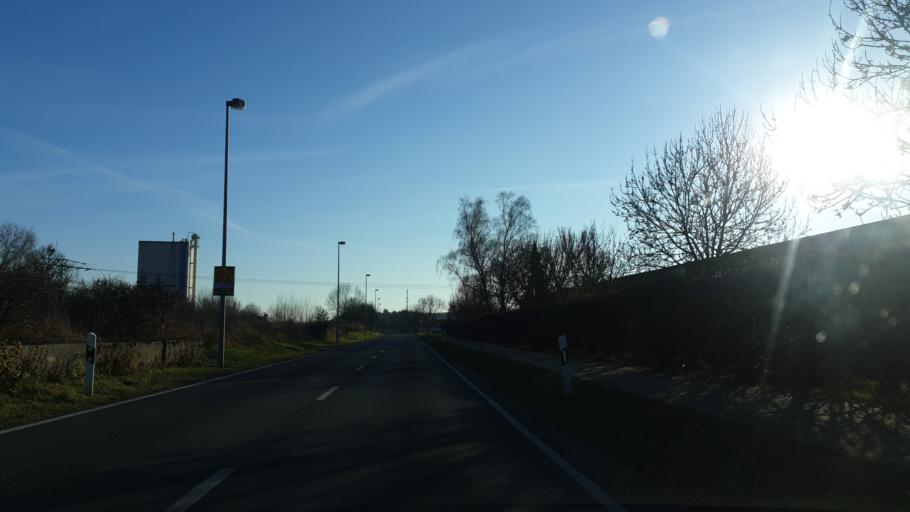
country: DE
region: Thuringia
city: Hartmannsdorf
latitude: 50.9722
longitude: 11.9819
